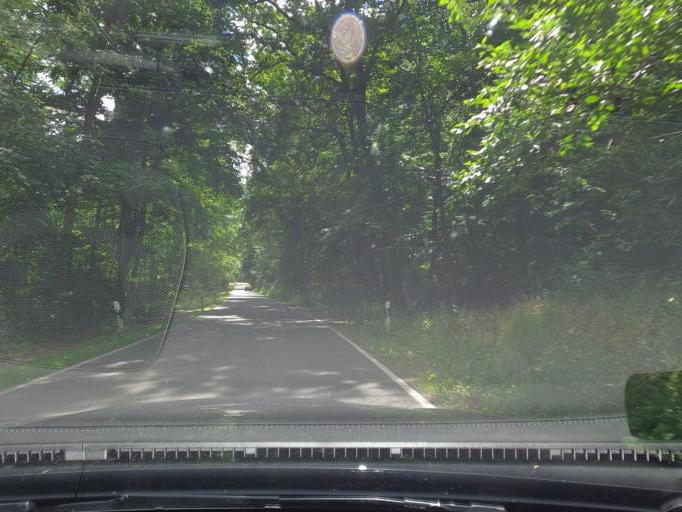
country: DE
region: Lower Saxony
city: Elbe
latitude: 52.1180
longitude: 10.2881
